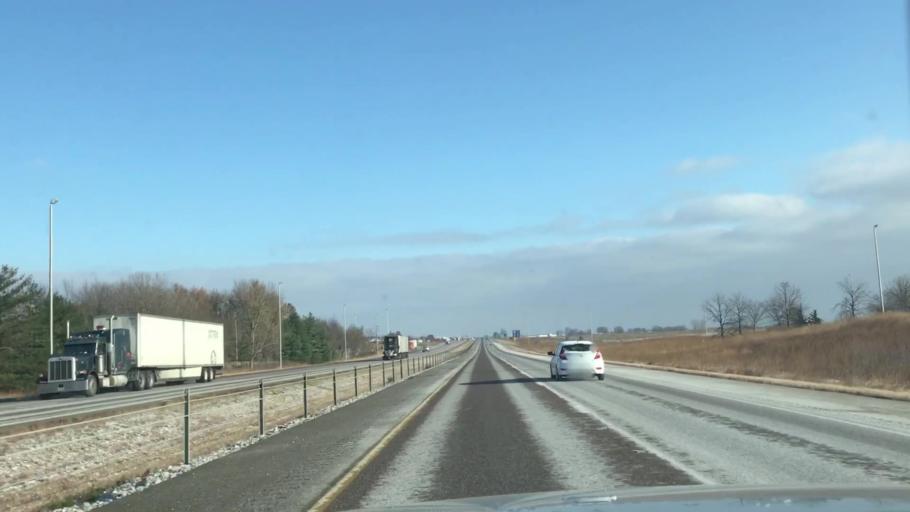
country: US
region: Illinois
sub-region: Madison County
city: Worden
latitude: 38.8655
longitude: -89.8546
